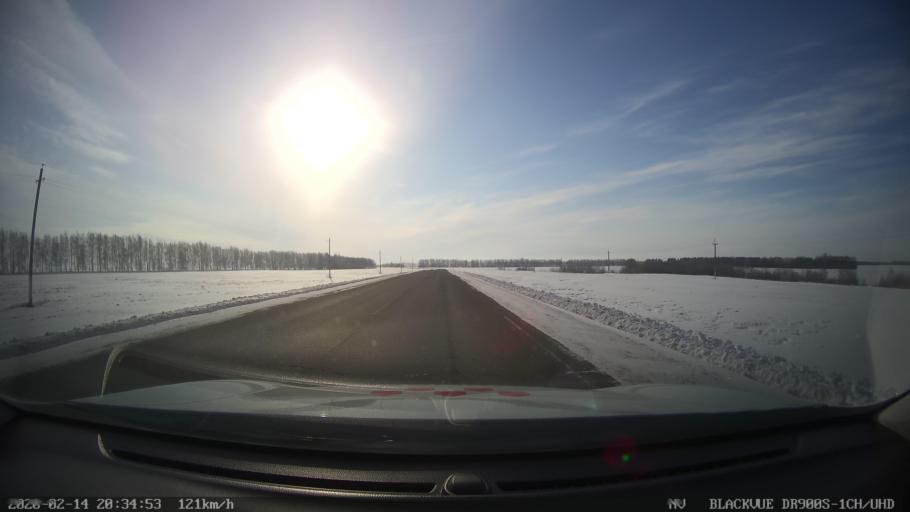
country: RU
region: Tatarstan
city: Kuybyshevskiy Zaton
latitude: 55.3917
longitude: 48.9791
